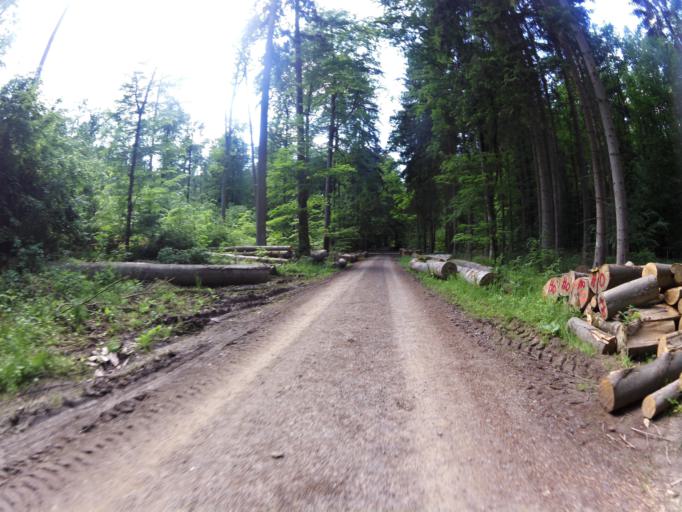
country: DE
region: Bavaria
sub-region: Regierungsbezirk Unterfranken
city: Uettingen
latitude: 49.7746
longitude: 9.7542
